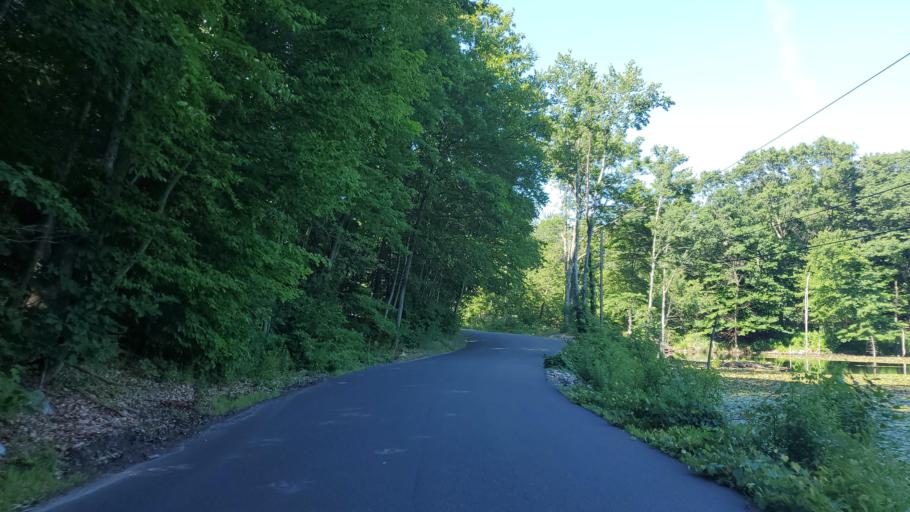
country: US
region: Connecticut
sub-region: Fairfield County
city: Newtown
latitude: 41.3360
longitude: -73.2924
